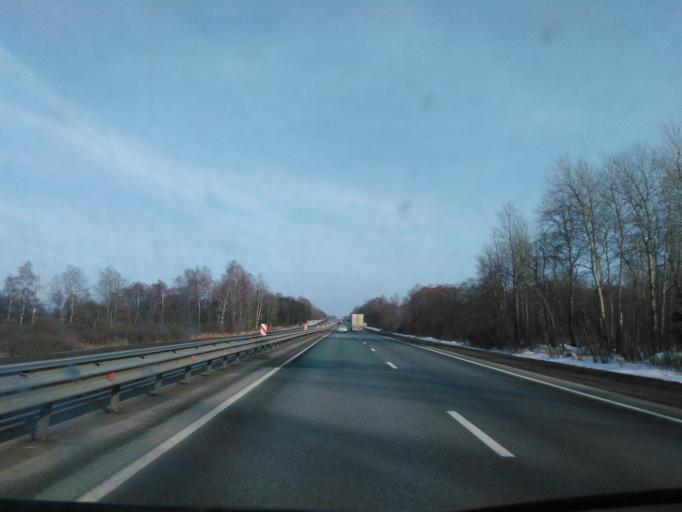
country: RU
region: Smolensk
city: Kholm-Zhirkovskiy
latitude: 55.1837
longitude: 33.6963
